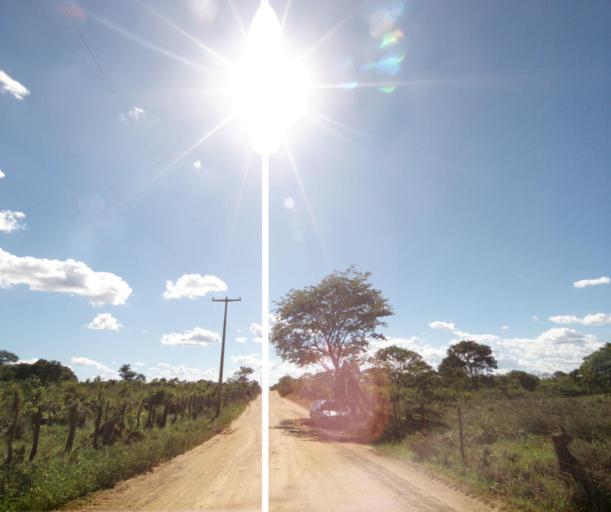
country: BR
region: Bahia
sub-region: Carinhanha
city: Carinhanha
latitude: -14.1802
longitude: -44.5131
